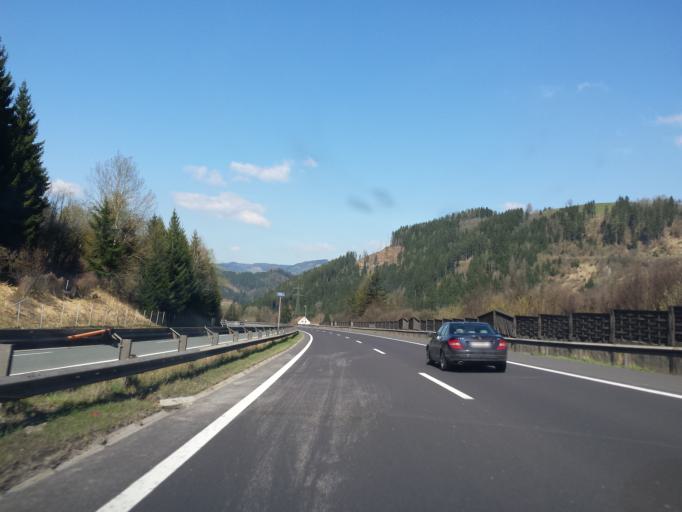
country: AT
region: Styria
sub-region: Politischer Bezirk Leoben
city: Sankt Michael in Obersteiermark
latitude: 47.3167
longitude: 15.0504
